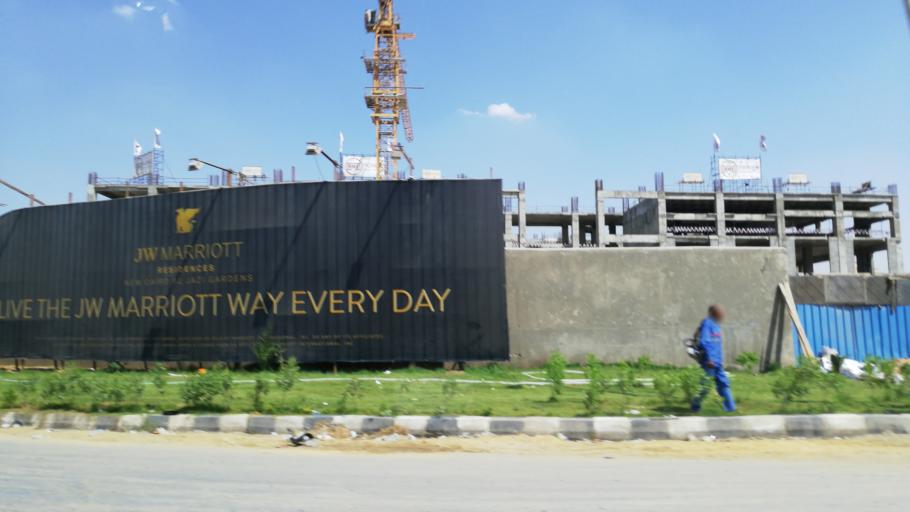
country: EG
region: Muhafazat al Qalyubiyah
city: Al Khankah
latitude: 30.0357
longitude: 31.4752
